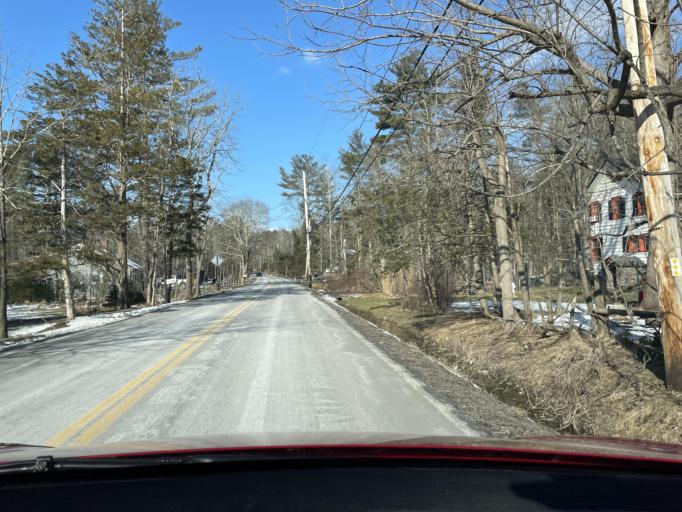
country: US
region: New York
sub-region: Ulster County
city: Woodstock
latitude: 42.0495
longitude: -74.1190
